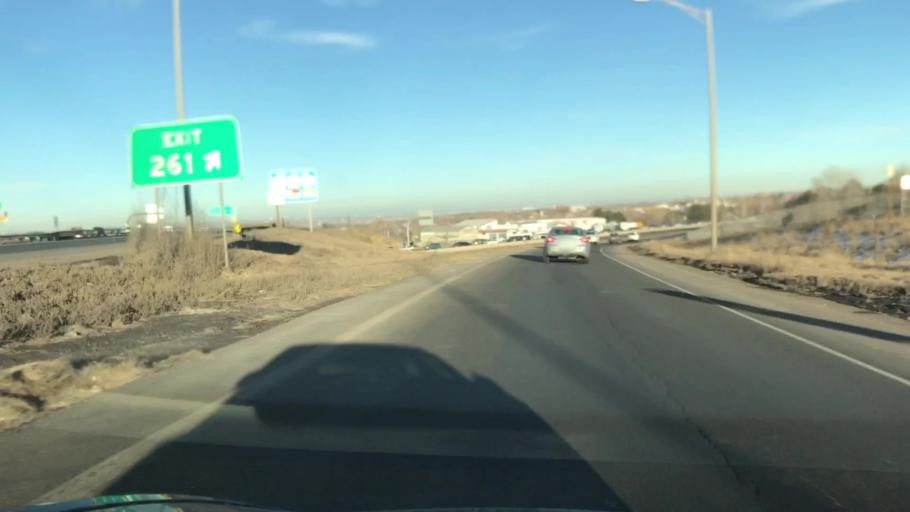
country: US
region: Colorado
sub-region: Jefferson County
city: West Pleasant View
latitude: 39.7244
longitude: -105.1801
